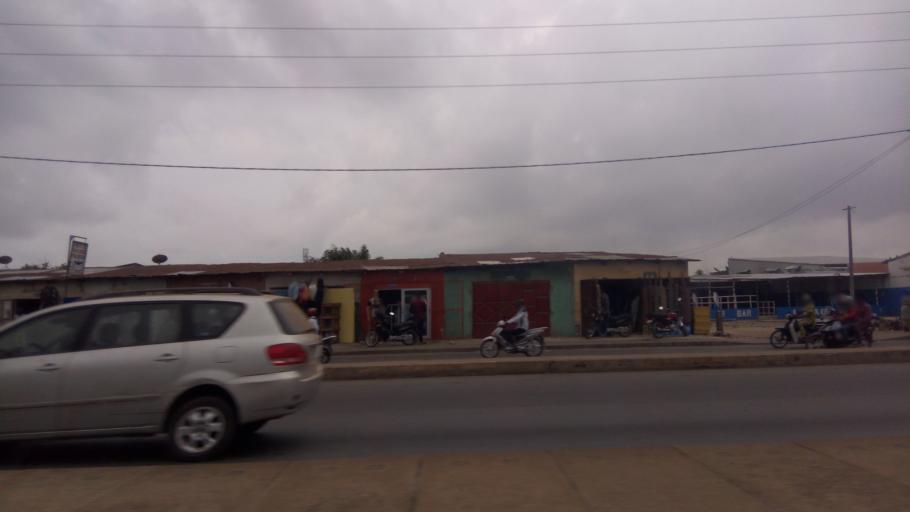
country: BJ
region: Atlantique
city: Abomey-Calavi
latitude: 6.3889
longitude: 2.3613
